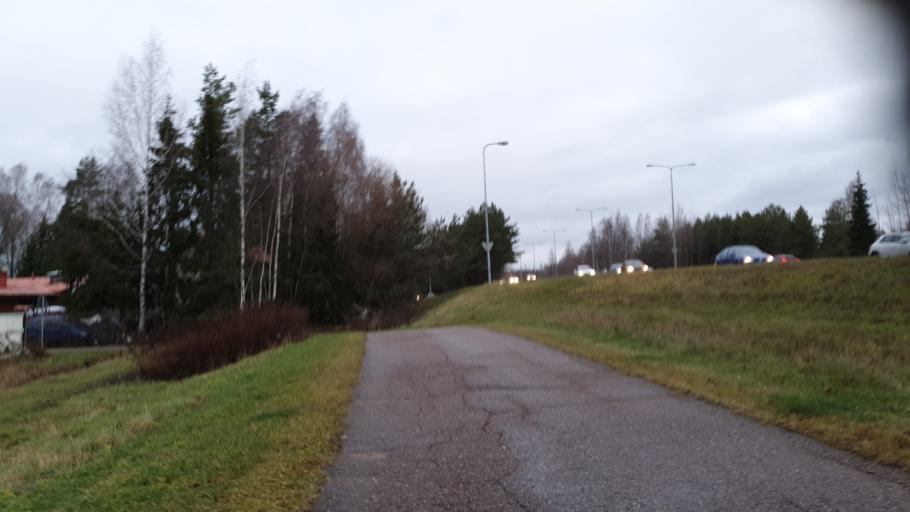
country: FI
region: Uusimaa
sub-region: Helsinki
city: Teekkarikylae
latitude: 60.2756
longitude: 24.8700
